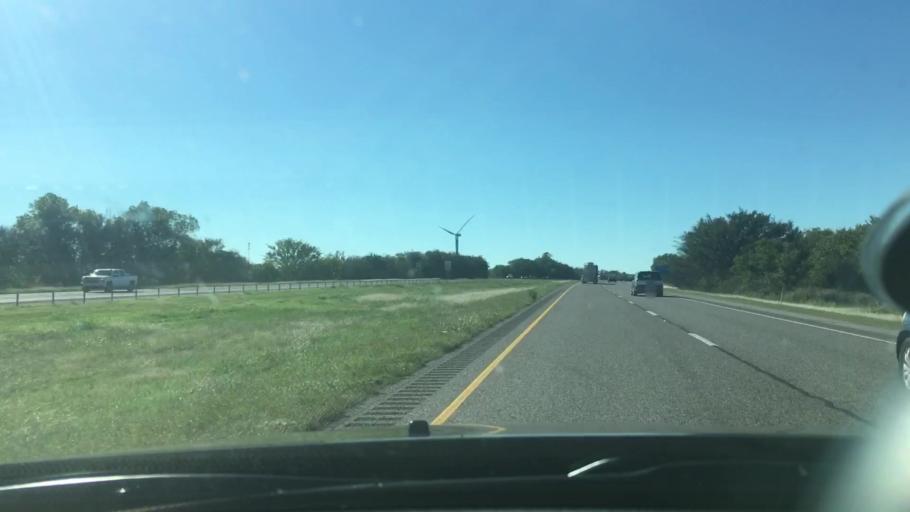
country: US
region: Oklahoma
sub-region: Murray County
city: Davis
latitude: 34.3910
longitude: -97.1420
